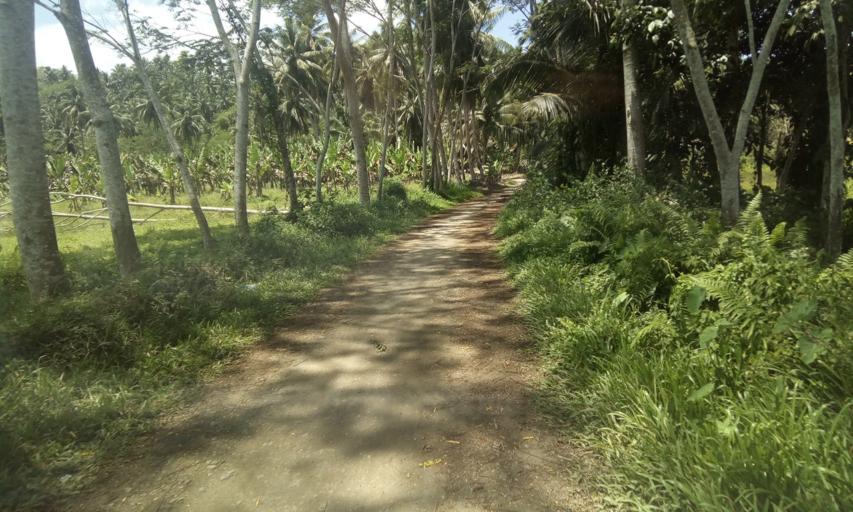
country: PH
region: Caraga
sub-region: Province of Agusan del Sur
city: Santa Josefa
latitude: 7.9545
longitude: 125.9957
